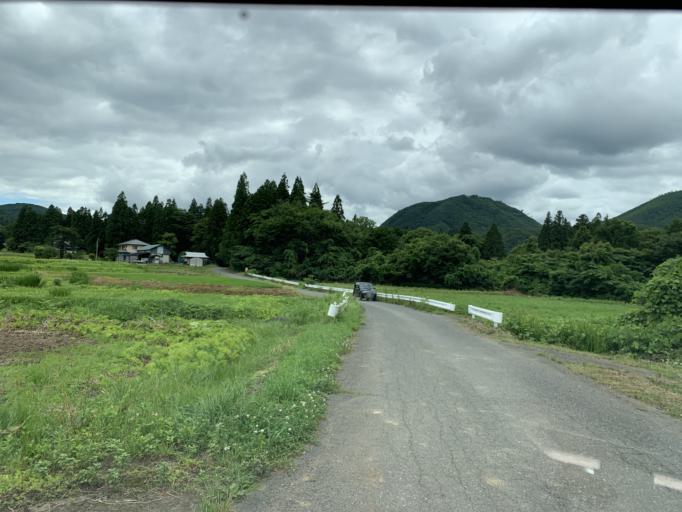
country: JP
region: Iwate
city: Ichinoseki
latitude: 38.9746
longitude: 140.9235
